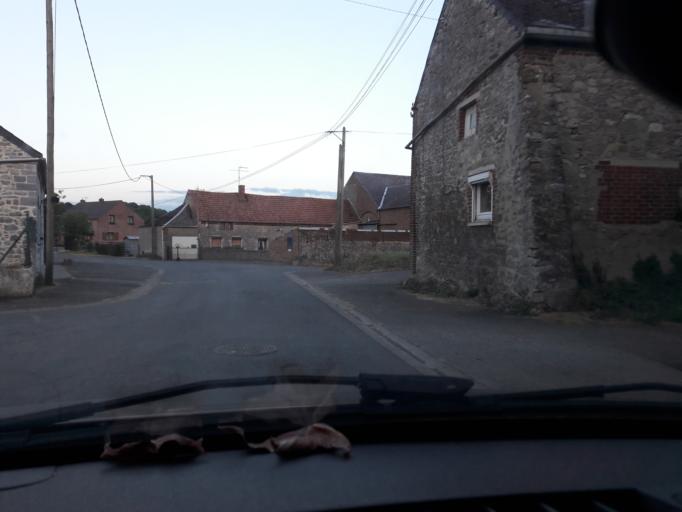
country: BE
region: Wallonia
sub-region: Province du Hainaut
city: Beaumont
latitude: 50.2643
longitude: 4.1845
